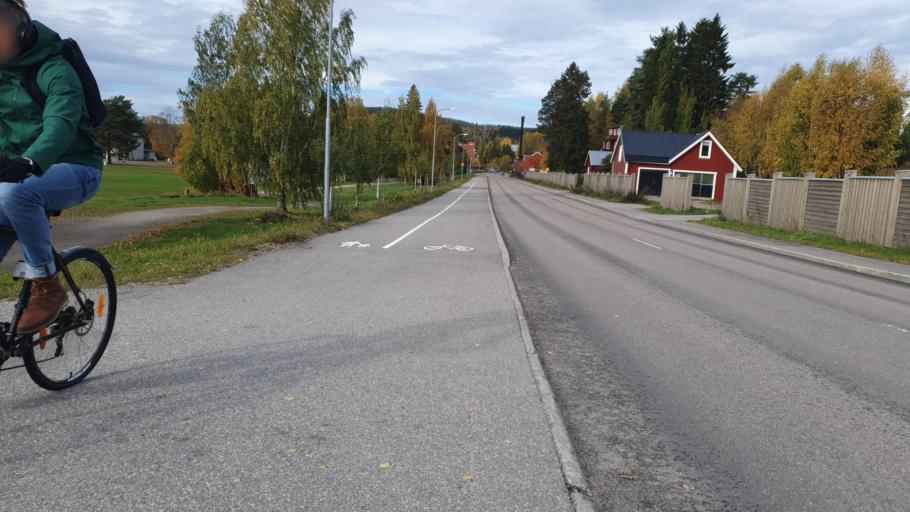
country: SE
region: Vaesternorrland
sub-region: Sundsvalls Kommun
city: Sundsvall
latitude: 62.4089
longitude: 17.2309
